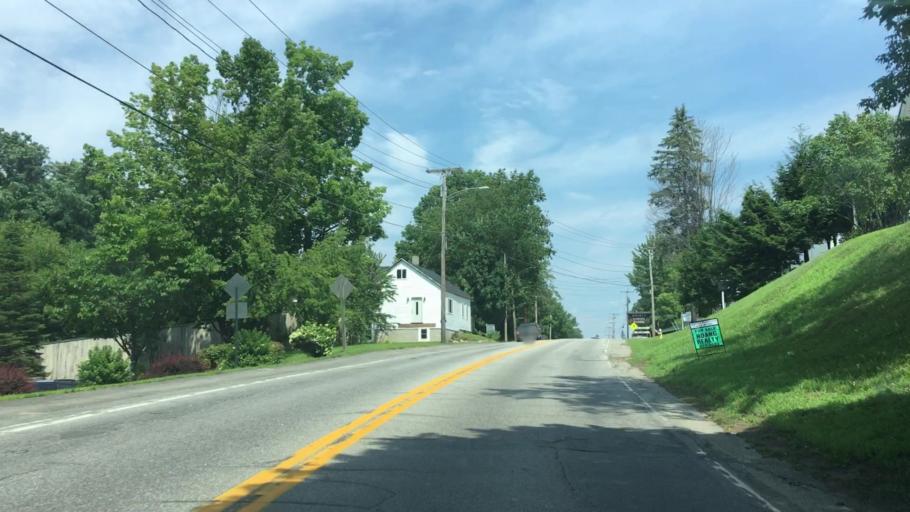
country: US
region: Maine
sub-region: Kennebec County
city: Hallowell
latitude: 44.2910
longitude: -69.7882
